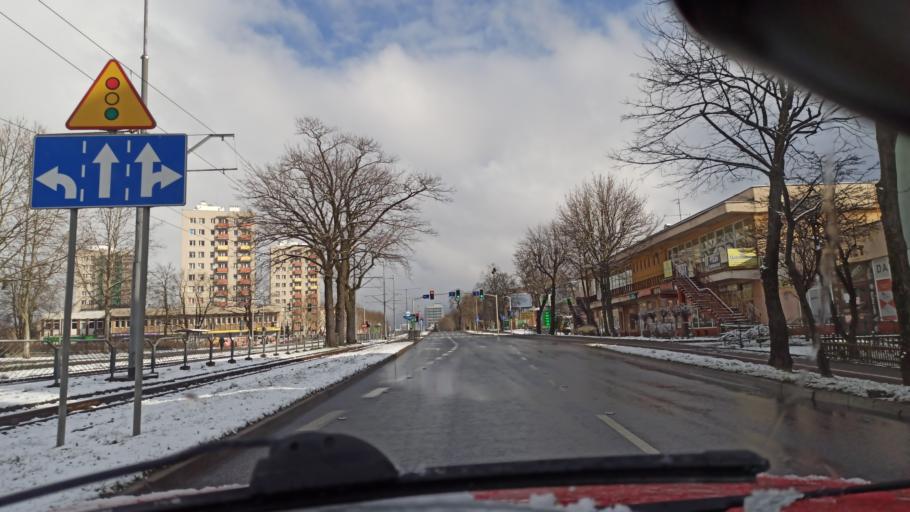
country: PL
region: Warmian-Masurian Voivodeship
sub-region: Powiat elblaski
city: Elblag
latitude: 54.1717
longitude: 19.4048
